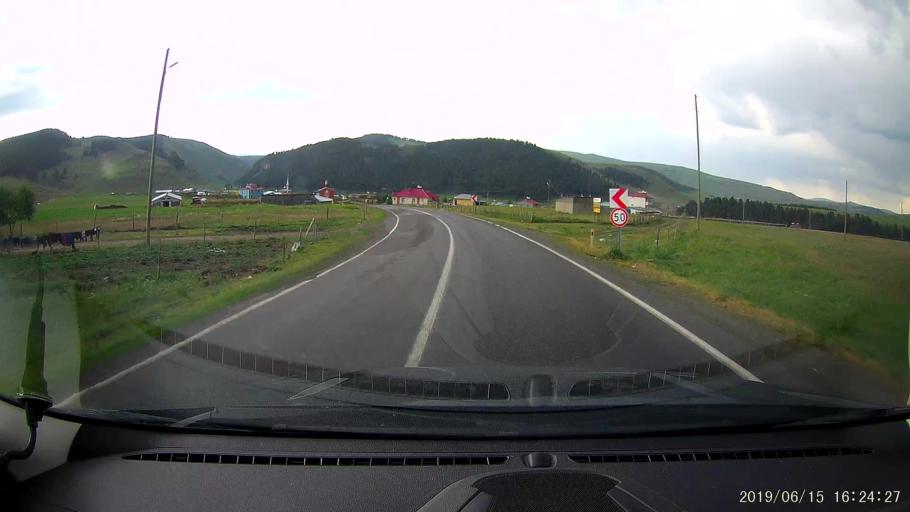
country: TR
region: Ardahan
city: Hanak
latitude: 41.1647
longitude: 42.8704
